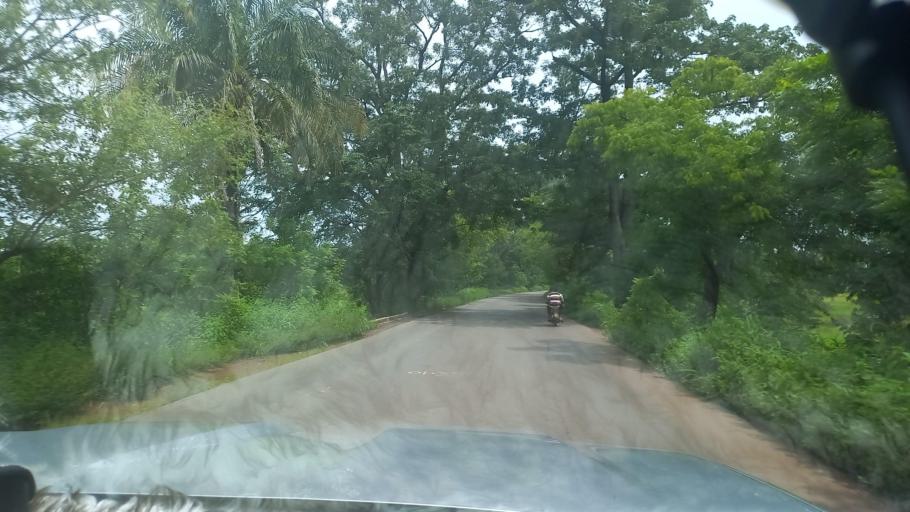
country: SN
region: Kolda
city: Marsassoum
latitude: 12.9571
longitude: -16.0034
